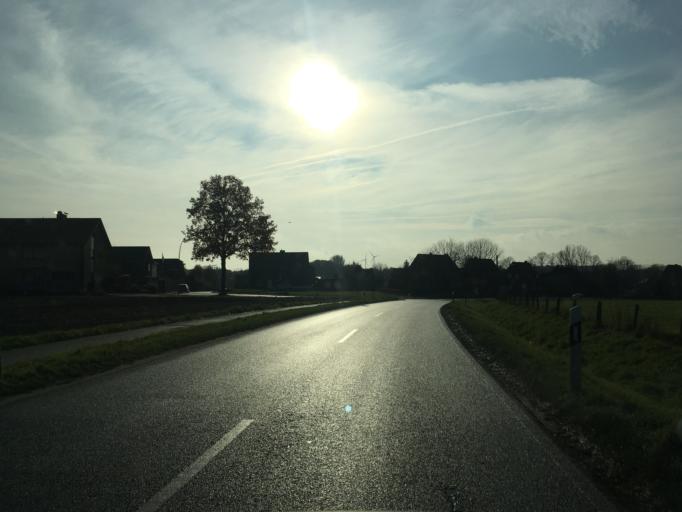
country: DE
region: North Rhine-Westphalia
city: Stadtlohn
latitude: 52.0012
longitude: 6.9356
